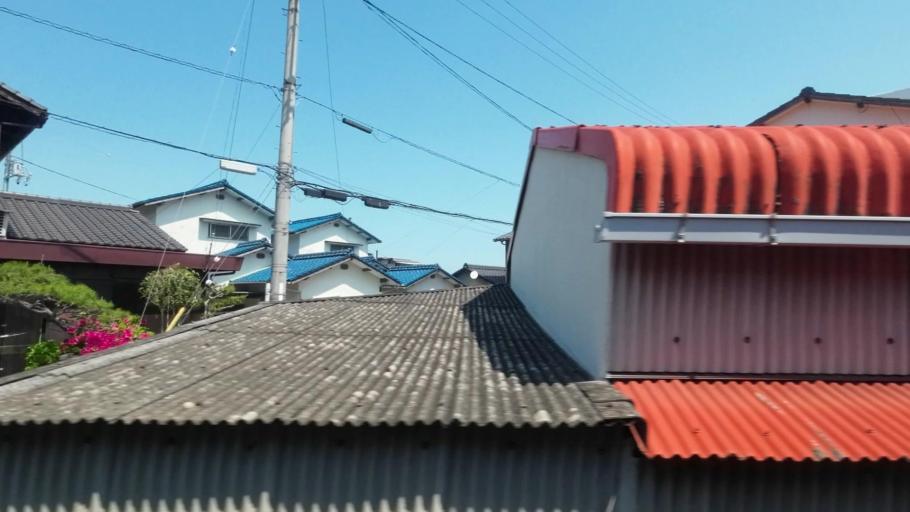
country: JP
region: Ehime
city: Hojo
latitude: 34.0983
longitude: 132.9667
